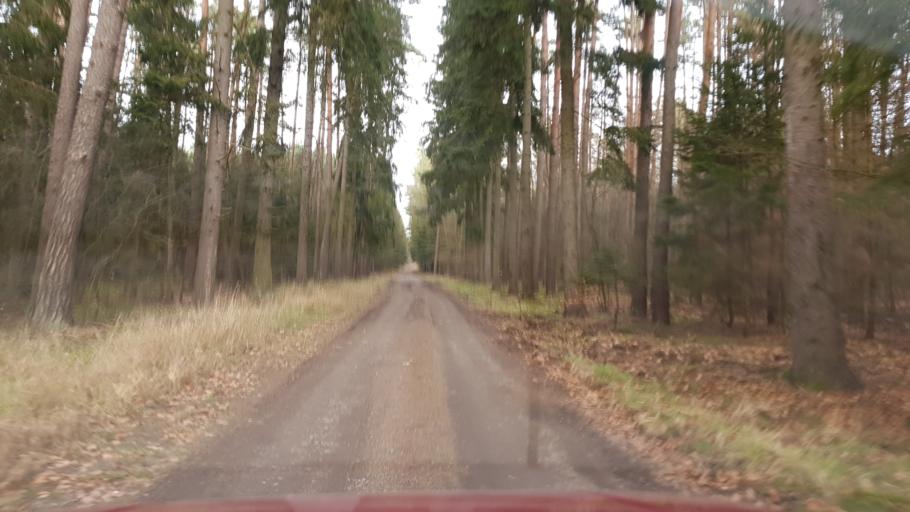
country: PL
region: Lubusz
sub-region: Powiat strzelecko-drezdenecki
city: Strzelce Krajenskie
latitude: 52.9089
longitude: 15.4079
